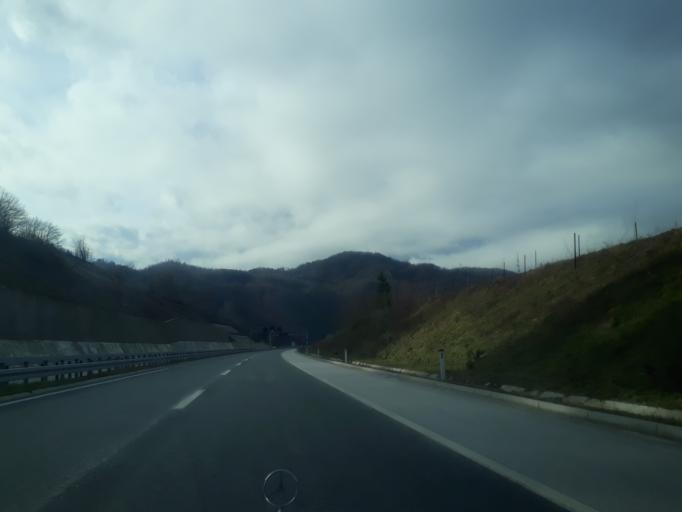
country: BA
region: Federation of Bosnia and Herzegovina
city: Polje
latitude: 43.8393
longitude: 18.1215
